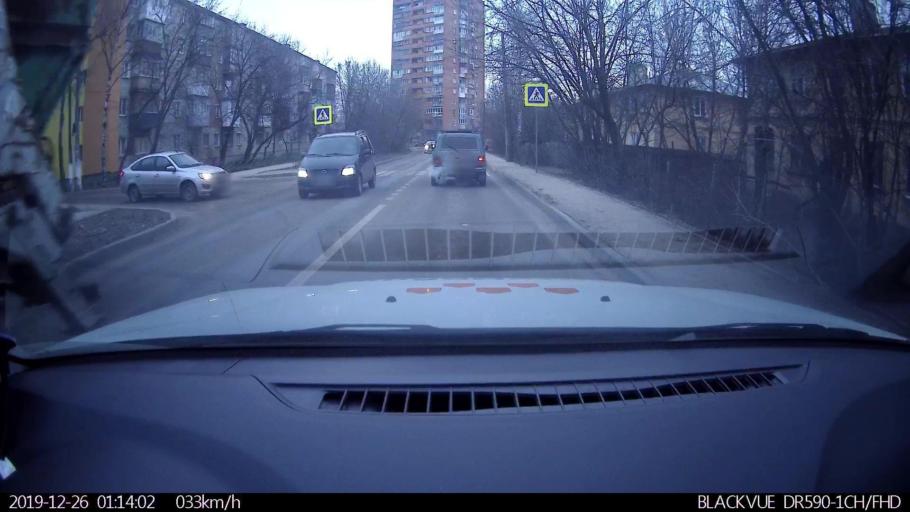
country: RU
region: Nizjnij Novgorod
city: Nizhniy Novgorod
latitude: 56.2752
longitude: 43.9089
